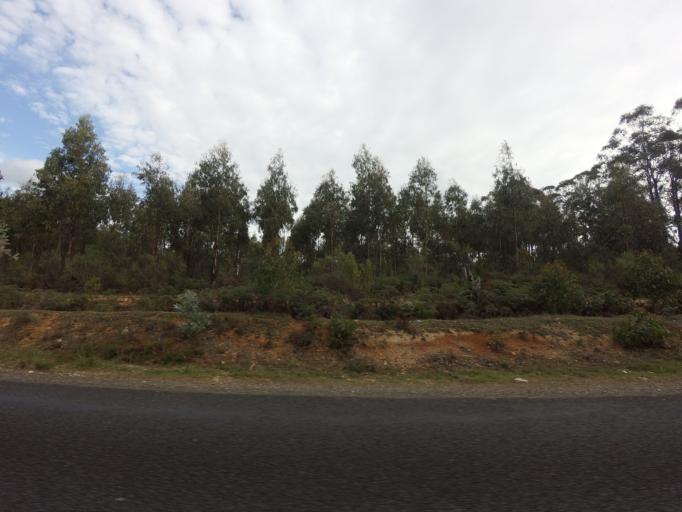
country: AU
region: Tasmania
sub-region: Meander Valley
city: Deloraine
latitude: -41.6123
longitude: 146.6870
